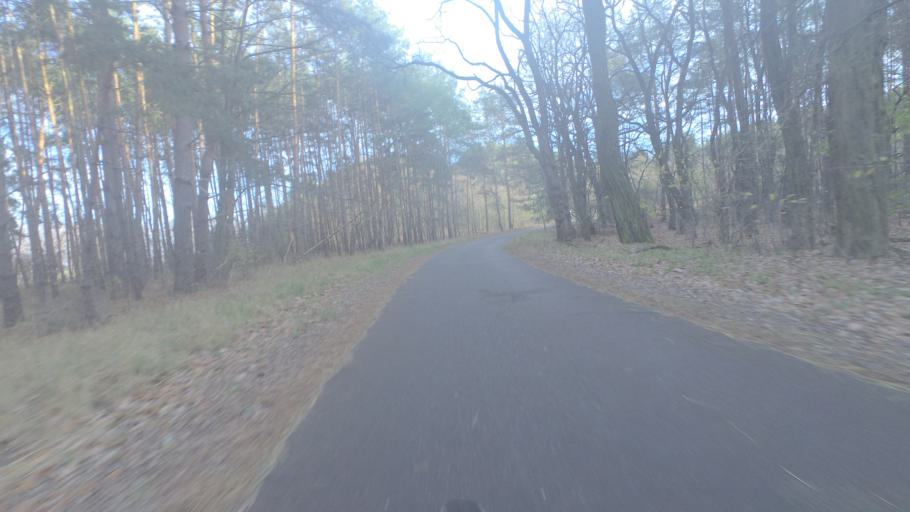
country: DE
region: Brandenburg
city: Zossen
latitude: 52.2200
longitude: 13.4870
